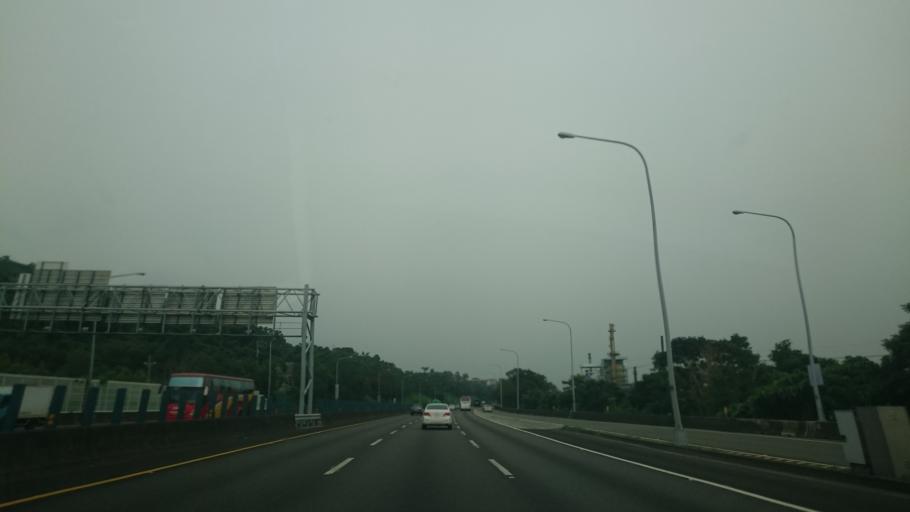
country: TW
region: Taiwan
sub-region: Changhua
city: Chang-hua
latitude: 24.1181
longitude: 120.5870
